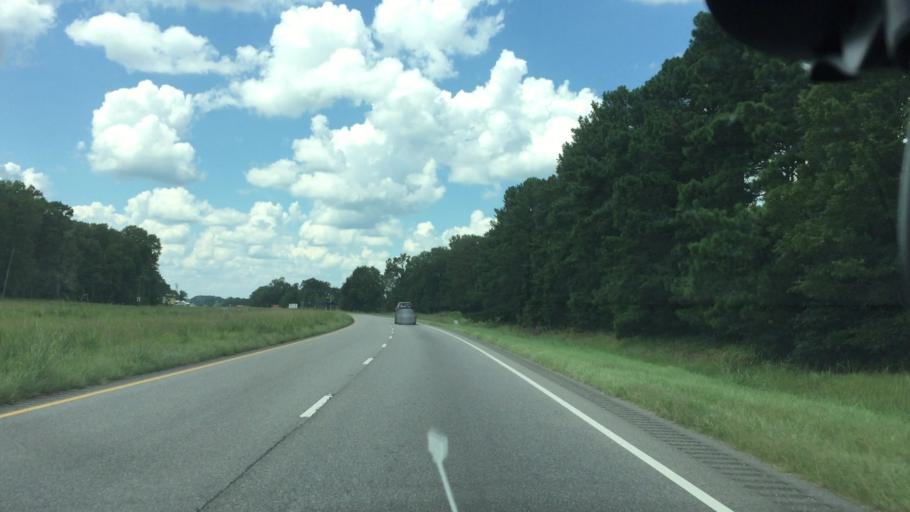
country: US
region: Alabama
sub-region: Montgomery County
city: Taylor
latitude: 32.0413
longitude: -86.0343
